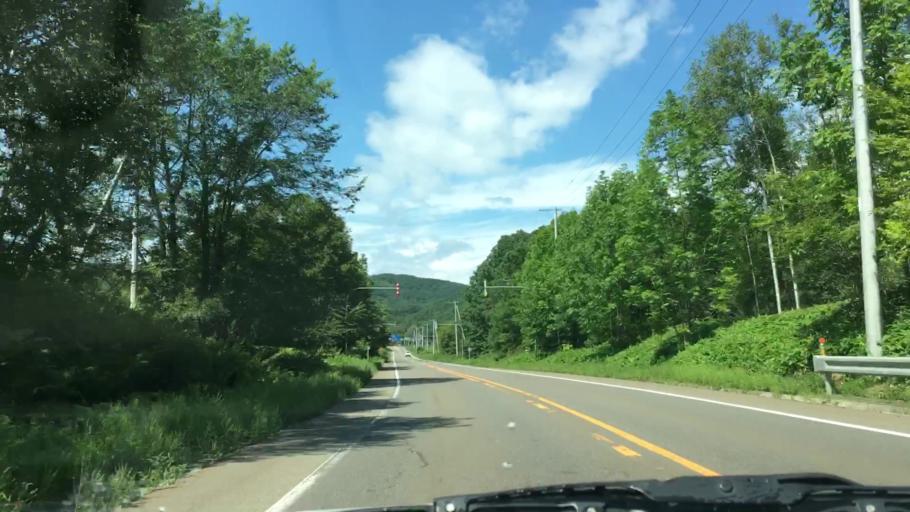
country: JP
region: Hokkaido
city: Otofuke
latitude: 43.2455
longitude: 143.4842
